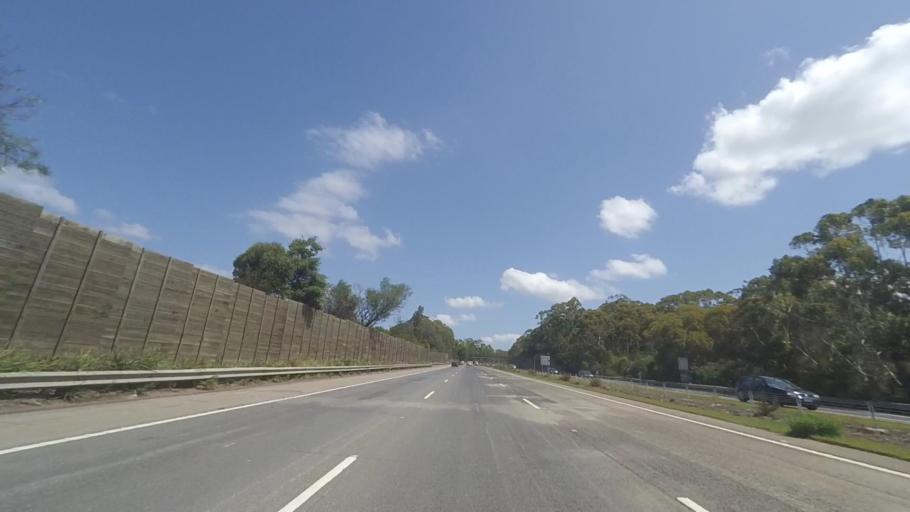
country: AU
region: New South Wales
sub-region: Hornsby Shire
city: Berowra
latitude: -33.6507
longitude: 151.1380
